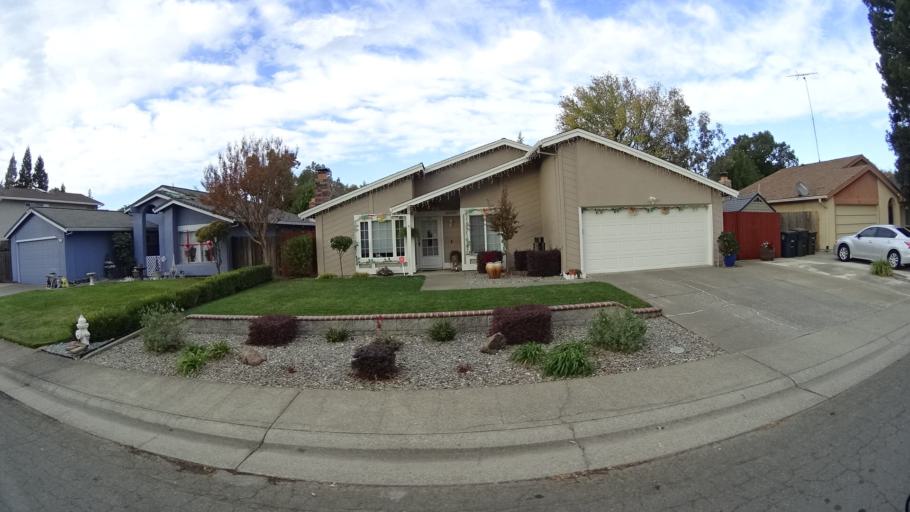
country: US
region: California
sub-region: Sacramento County
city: Citrus Heights
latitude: 38.7146
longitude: -121.2509
